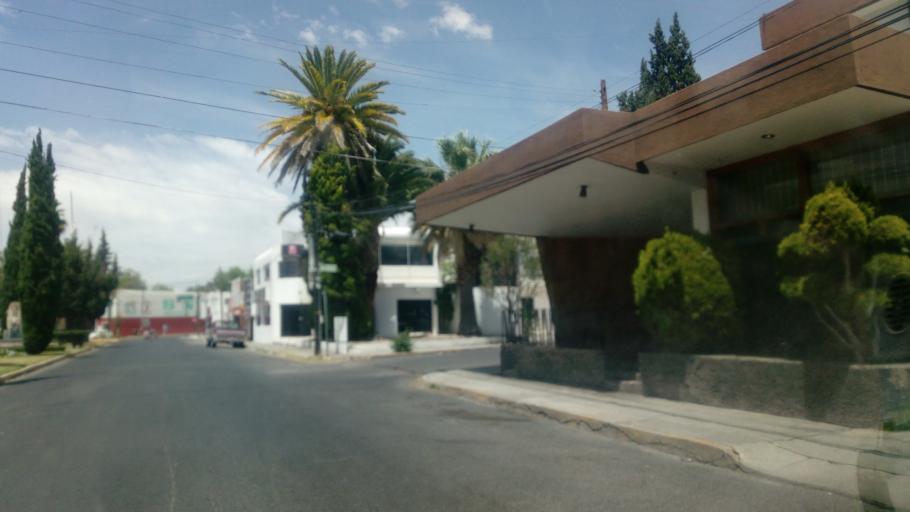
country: MX
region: Durango
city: Victoria de Durango
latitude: 24.0248
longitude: -104.6792
